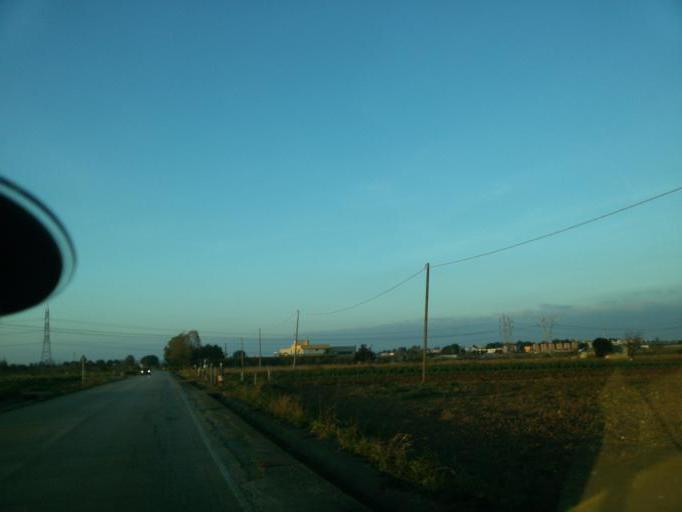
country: IT
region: Apulia
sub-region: Provincia di Brindisi
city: La Rosa
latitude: 40.5985
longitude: 17.9466
